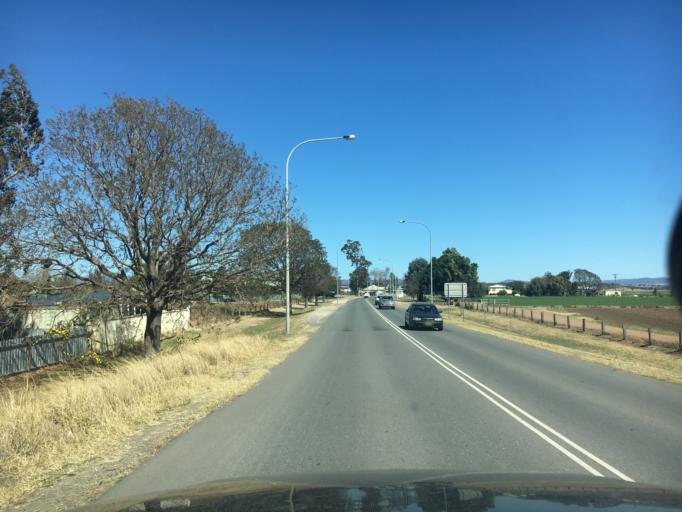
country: AU
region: New South Wales
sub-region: Singleton
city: Singleton
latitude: -32.5718
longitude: 151.1634
